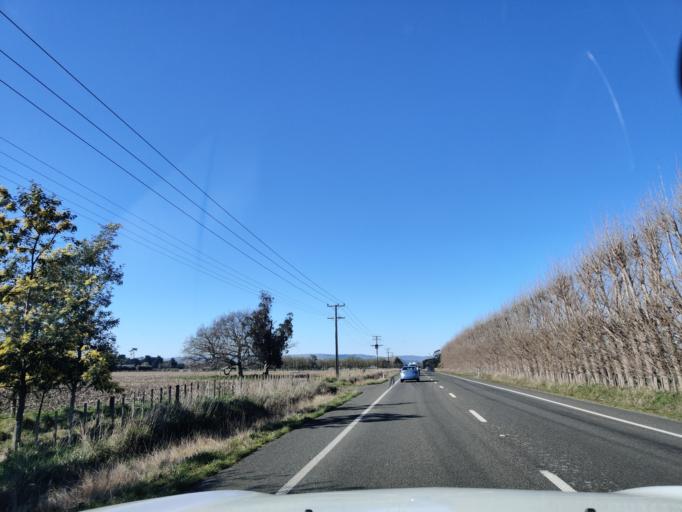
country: NZ
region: Manawatu-Wanganui
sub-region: Palmerston North City
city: Palmerston North
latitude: -40.2991
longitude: 175.5775
